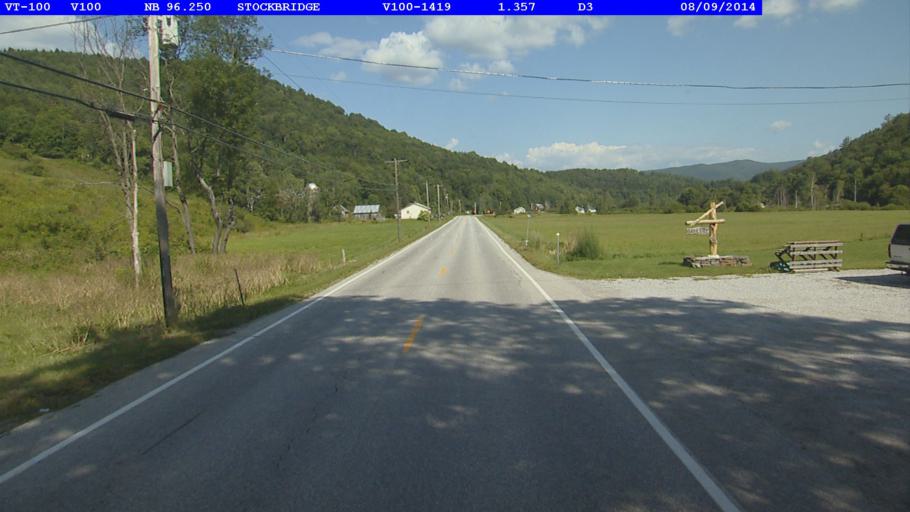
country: US
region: Vermont
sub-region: Orange County
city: Randolph
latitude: 43.7767
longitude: -72.7727
